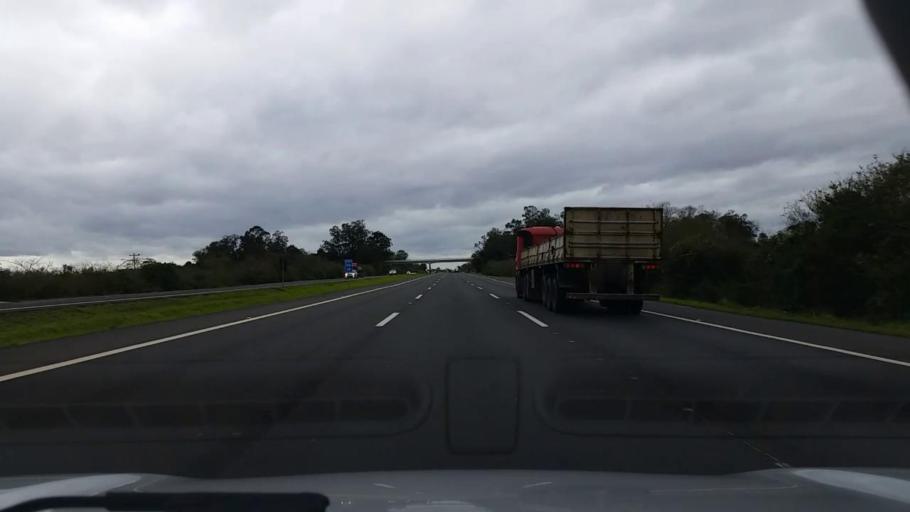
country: BR
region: Rio Grande do Sul
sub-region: Rolante
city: Rolante
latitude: -29.8833
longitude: -50.5439
